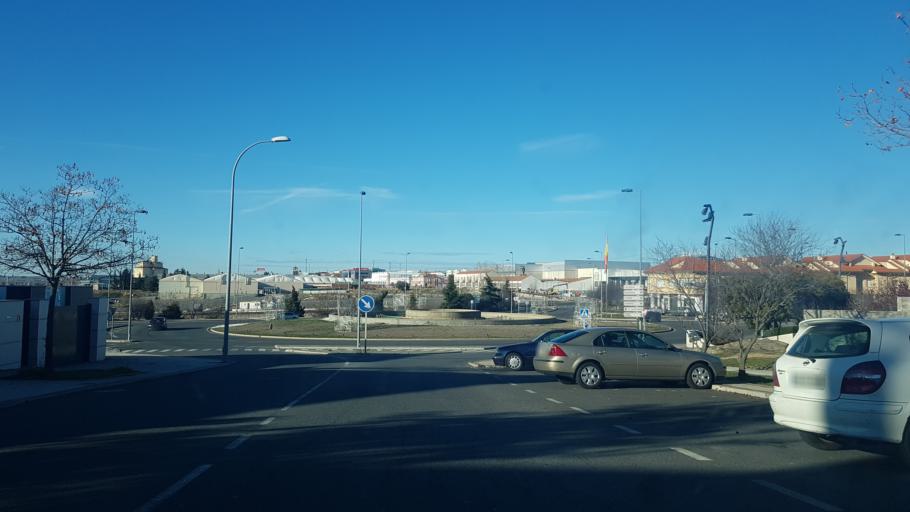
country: ES
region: Castille and Leon
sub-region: Provincia de Avila
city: Avila
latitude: 40.6590
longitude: -4.6790
